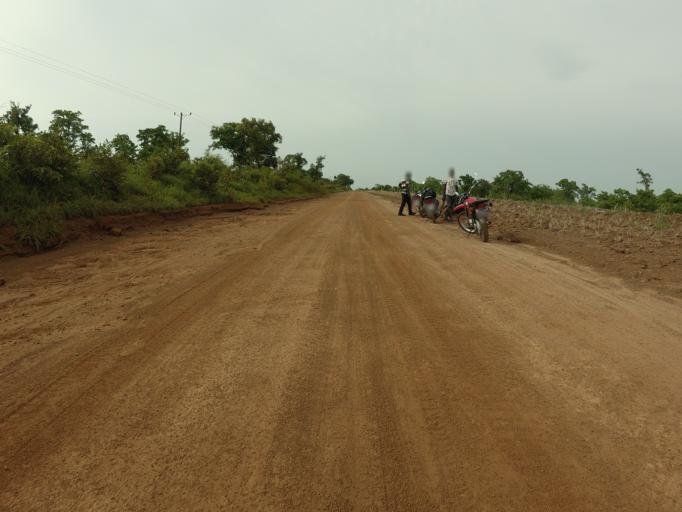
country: GH
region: Northern
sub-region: Yendi
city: Yendi
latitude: 9.6499
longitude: -0.0697
